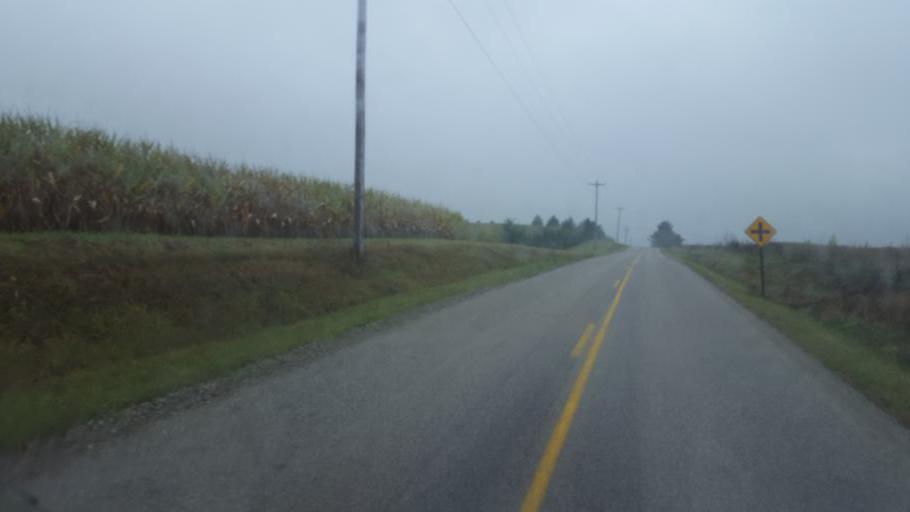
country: US
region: Ohio
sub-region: Richland County
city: Lexington
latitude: 40.6010
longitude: -82.6087
